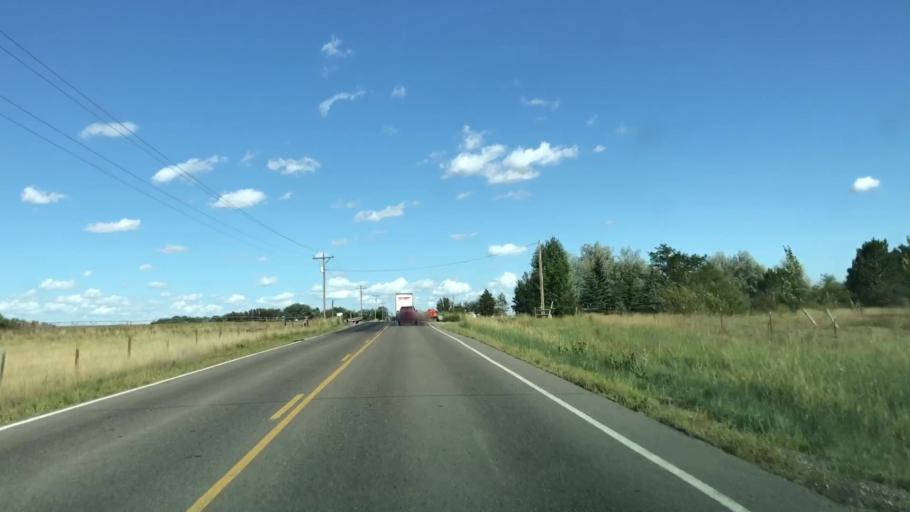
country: US
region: Colorado
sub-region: Larimer County
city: Wellington
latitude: 40.7547
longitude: -105.0842
